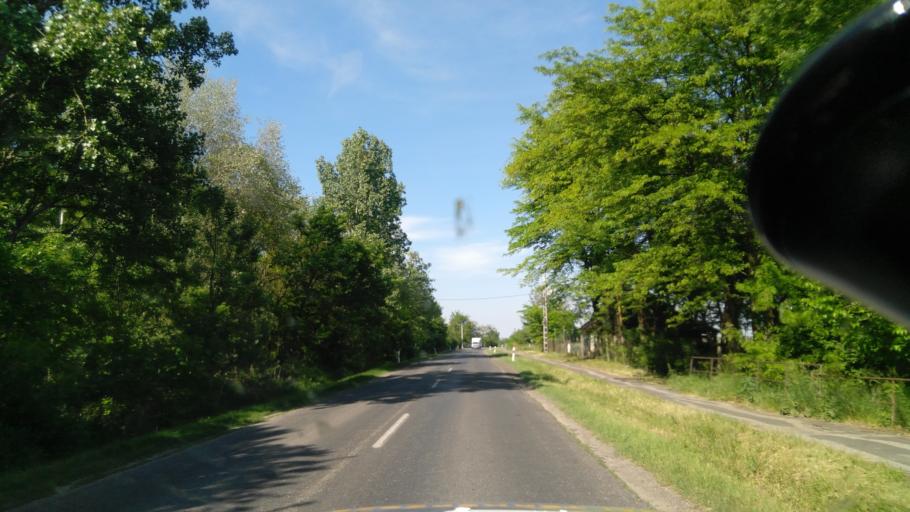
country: HU
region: Bekes
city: Sarkad
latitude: 46.7235
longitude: 21.3394
